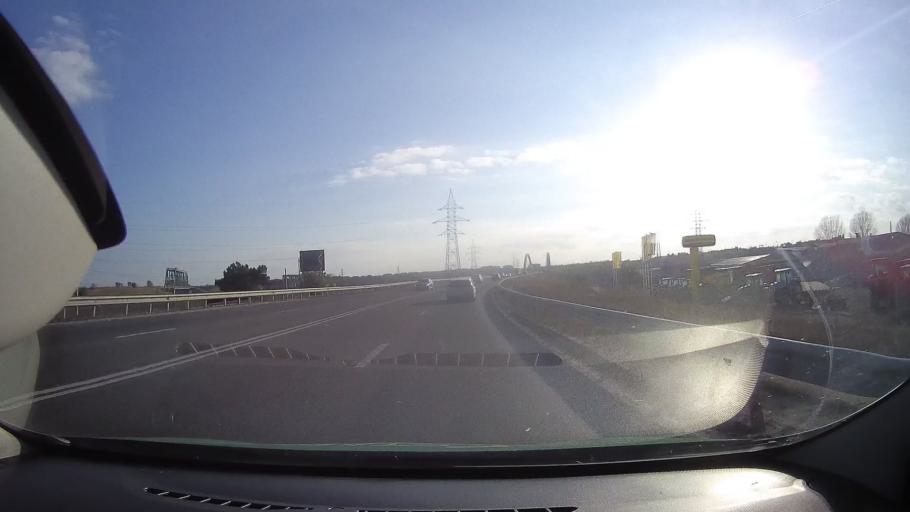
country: RO
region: Constanta
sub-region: Comuna Ovidiu
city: Ovidiu
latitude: 44.2719
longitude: 28.5577
